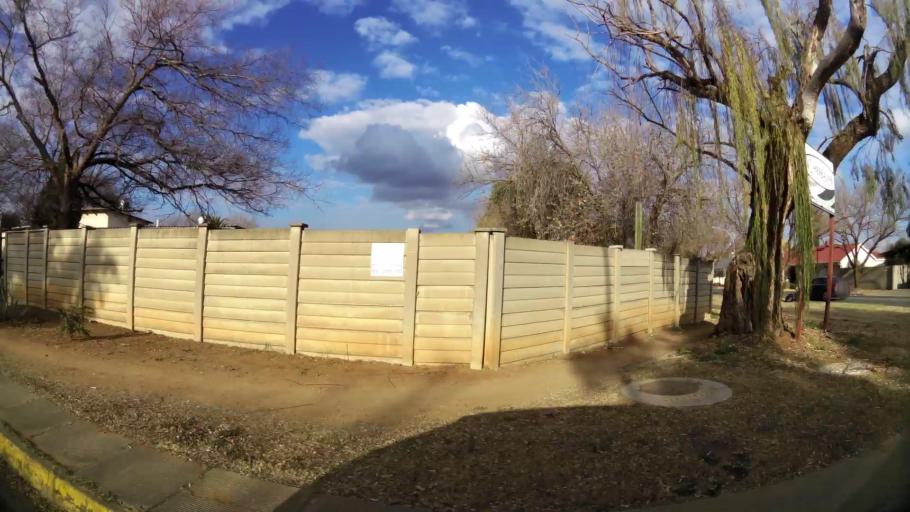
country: ZA
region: Orange Free State
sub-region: Mangaung Metropolitan Municipality
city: Bloemfontein
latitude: -29.1026
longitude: 26.1972
